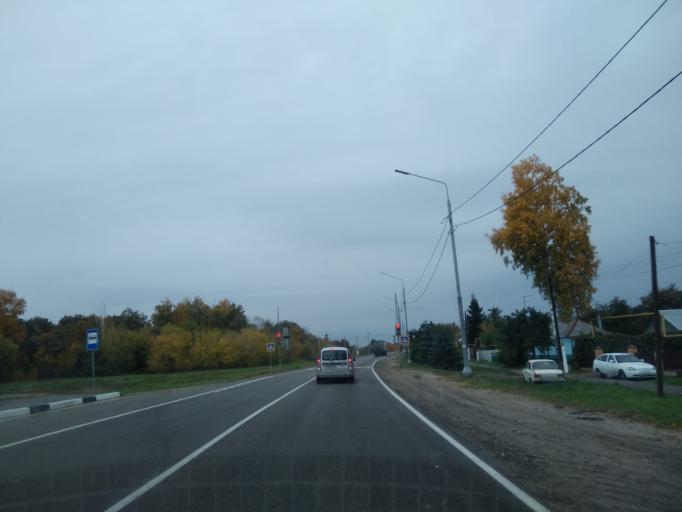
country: RU
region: Lipetsk
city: Zadonsk
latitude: 52.4190
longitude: 38.8482
